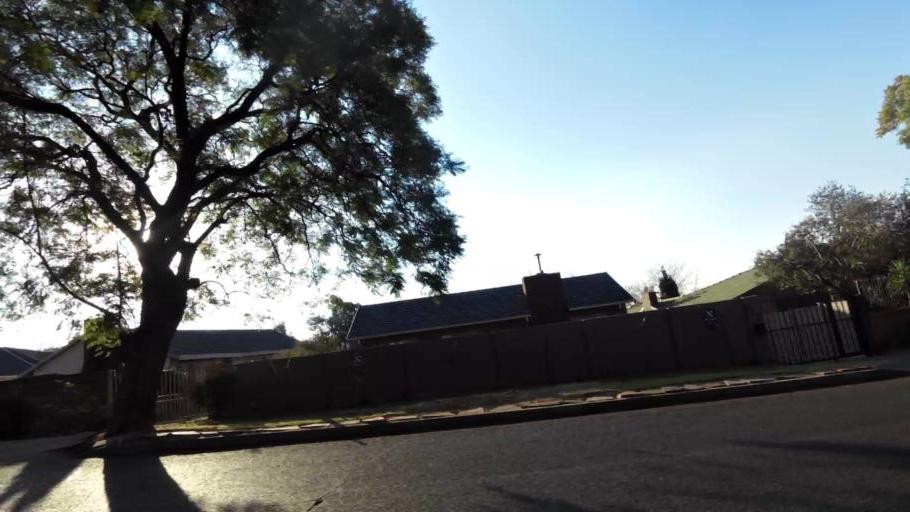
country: ZA
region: Gauteng
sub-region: City of Johannesburg Metropolitan Municipality
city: Johannesburg
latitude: -26.1580
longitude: 27.9878
